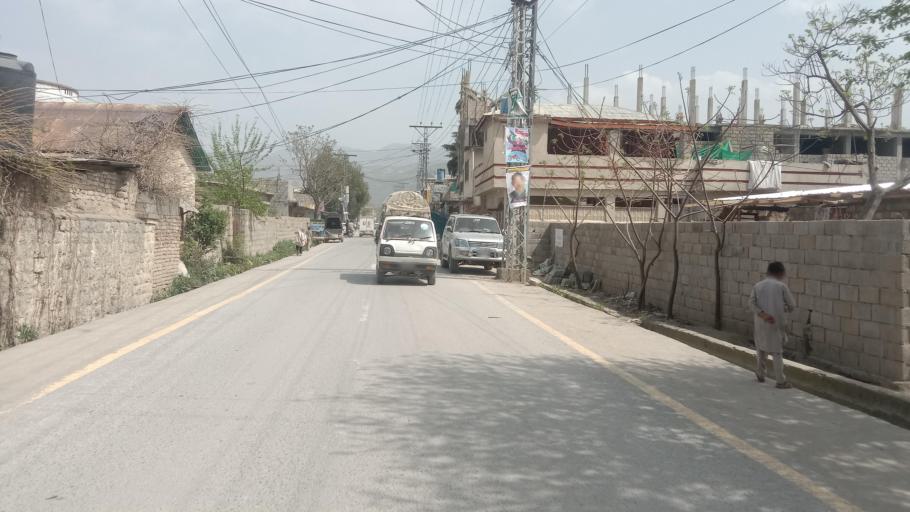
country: PK
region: Khyber Pakhtunkhwa
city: Abbottabad
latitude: 34.1621
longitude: 73.2557
